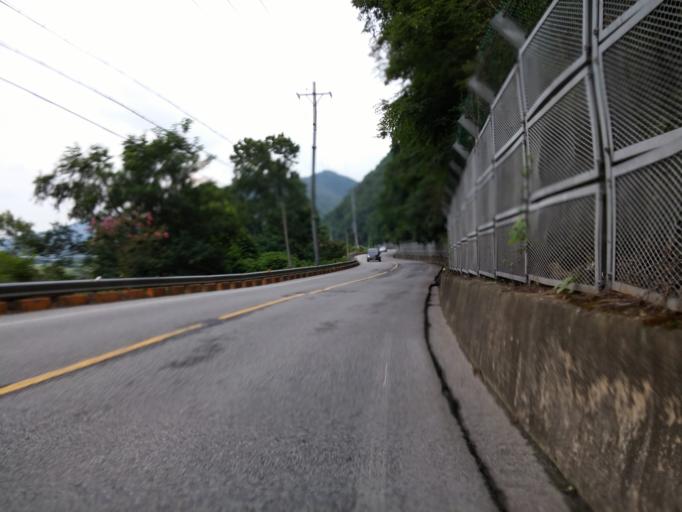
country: KR
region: Chungcheongnam-do
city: Gongju
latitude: 36.4369
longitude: 127.2016
